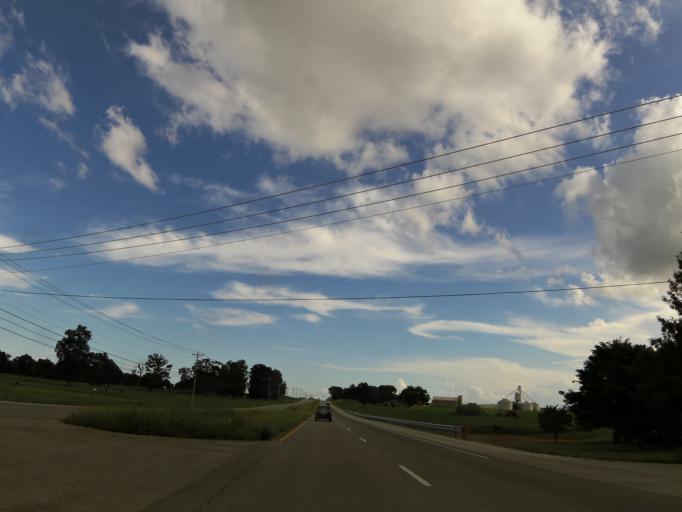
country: US
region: Kentucky
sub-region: Christian County
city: Oak Grove
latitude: 36.7410
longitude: -87.4660
